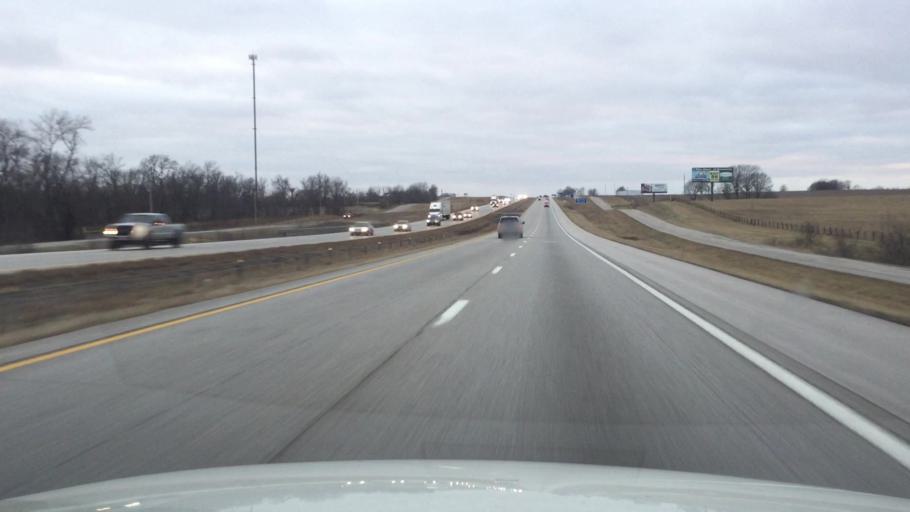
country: US
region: Missouri
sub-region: Saline County
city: Sweet Springs
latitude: 38.9764
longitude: -93.3960
